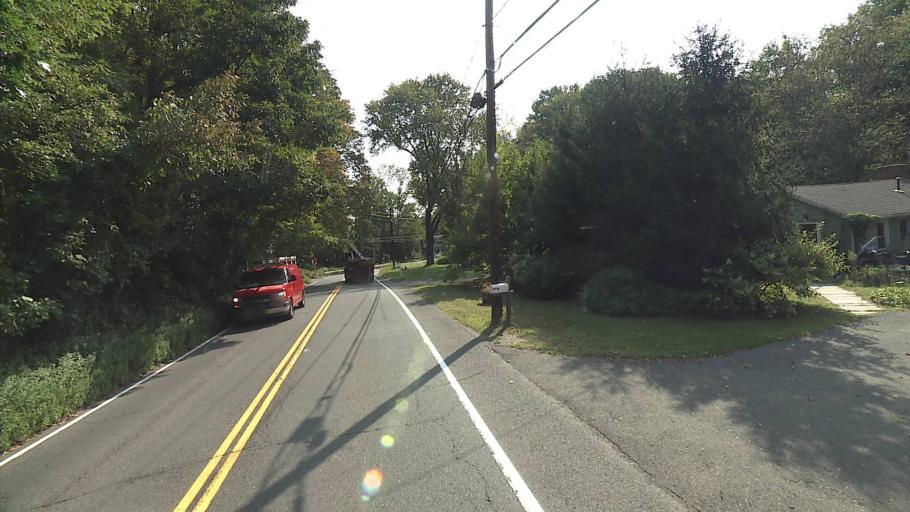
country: US
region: Connecticut
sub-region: Fairfield County
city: Bethel
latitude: 41.3226
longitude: -73.3579
